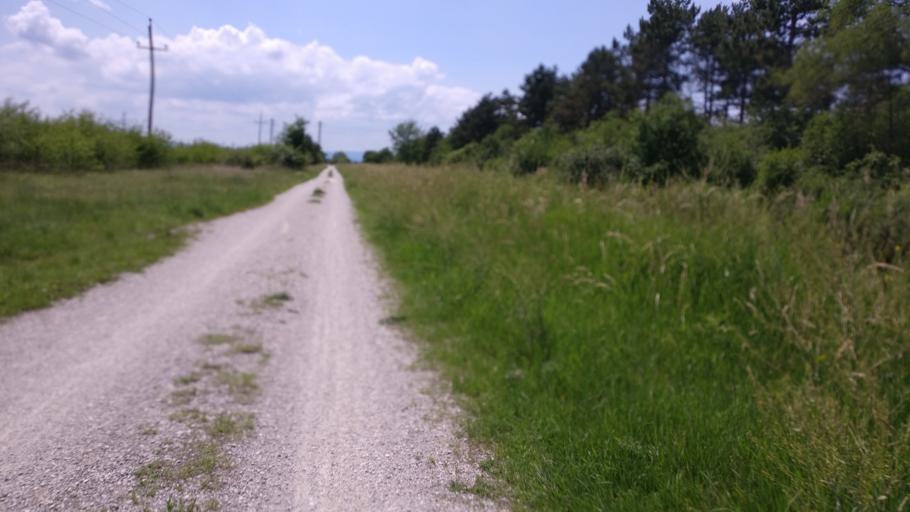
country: AT
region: Lower Austria
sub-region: Politischer Bezirk Wiener Neustadt
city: Lichtenworth
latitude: 47.8587
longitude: 16.2813
